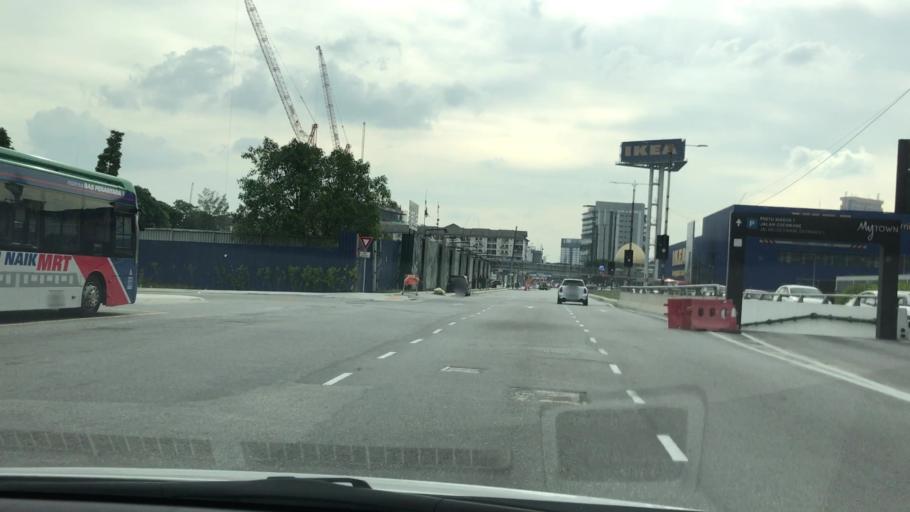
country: MY
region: Kuala Lumpur
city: Kuala Lumpur
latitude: 3.1335
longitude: 101.7227
